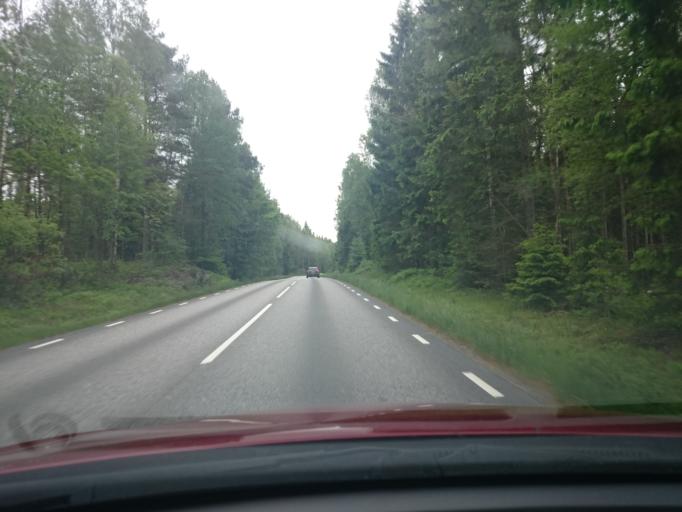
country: SE
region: Vaestra Goetaland
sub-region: Lerums Kommun
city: Stenkullen
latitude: 57.7573
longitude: 12.3181
